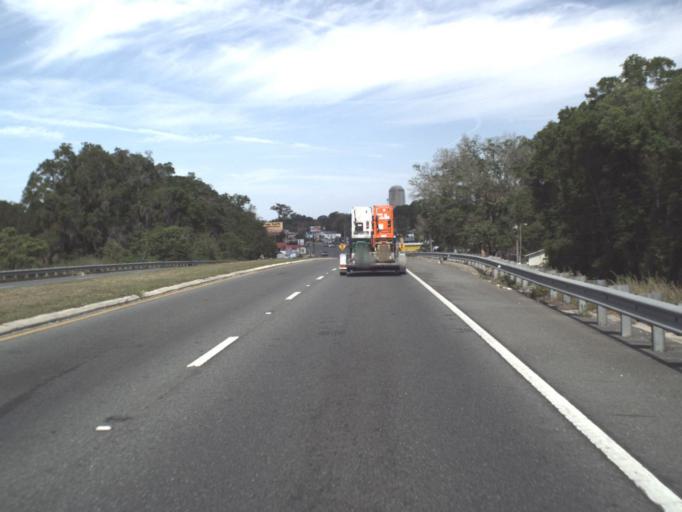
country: US
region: Florida
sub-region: Marion County
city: Belleview
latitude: 29.0560
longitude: -82.0447
